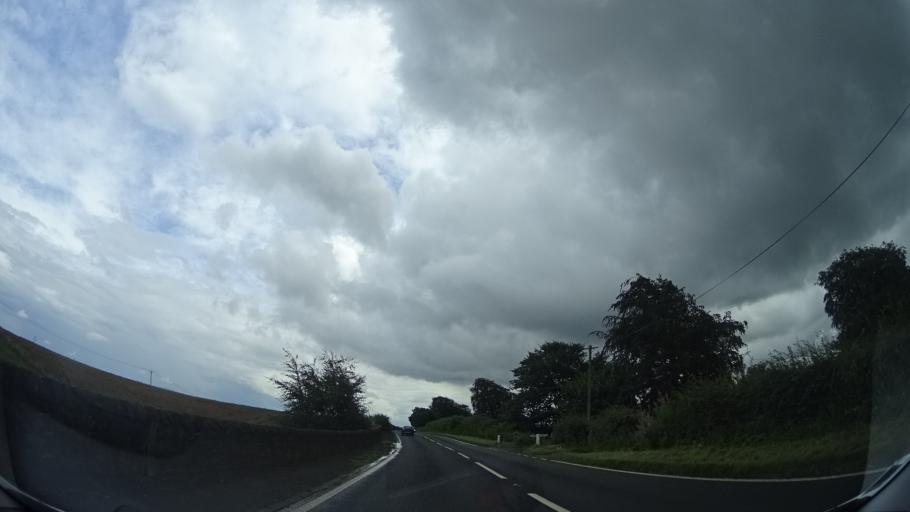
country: GB
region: Scotland
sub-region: Falkirk
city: Larbert
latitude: 56.0075
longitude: -3.8494
